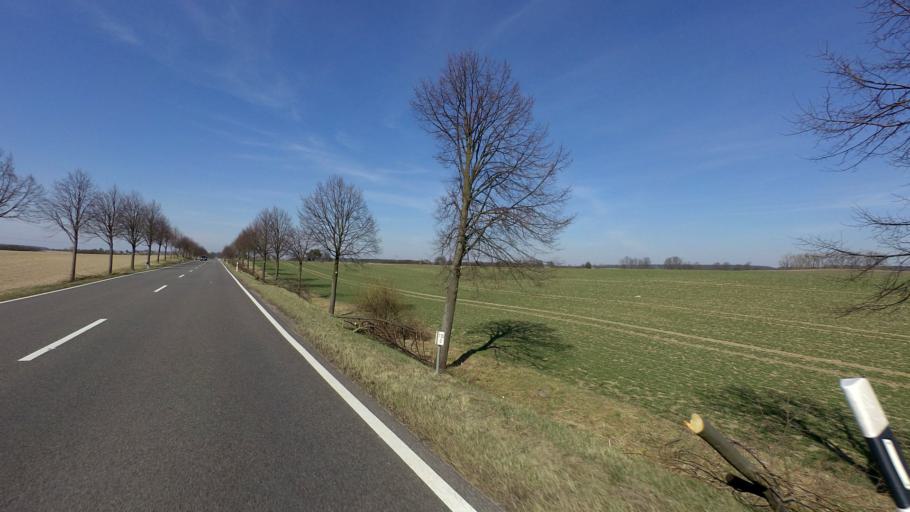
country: DE
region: Brandenburg
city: Buckow
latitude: 52.5842
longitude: 14.0297
